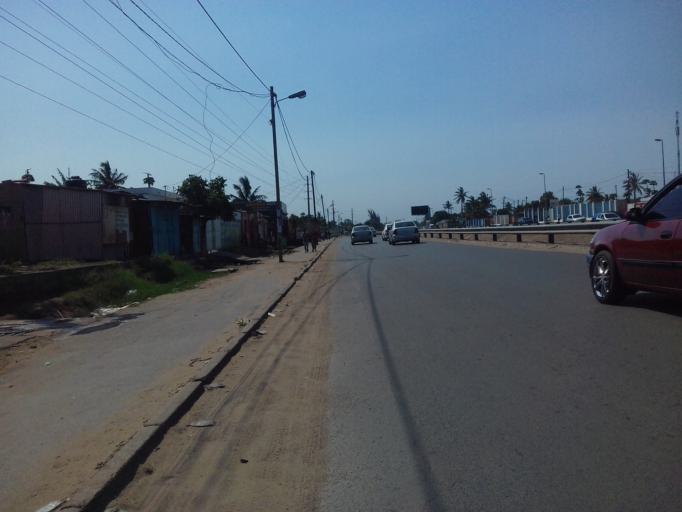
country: MZ
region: Maputo City
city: Maputo
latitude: -25.9469
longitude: 32.5778
